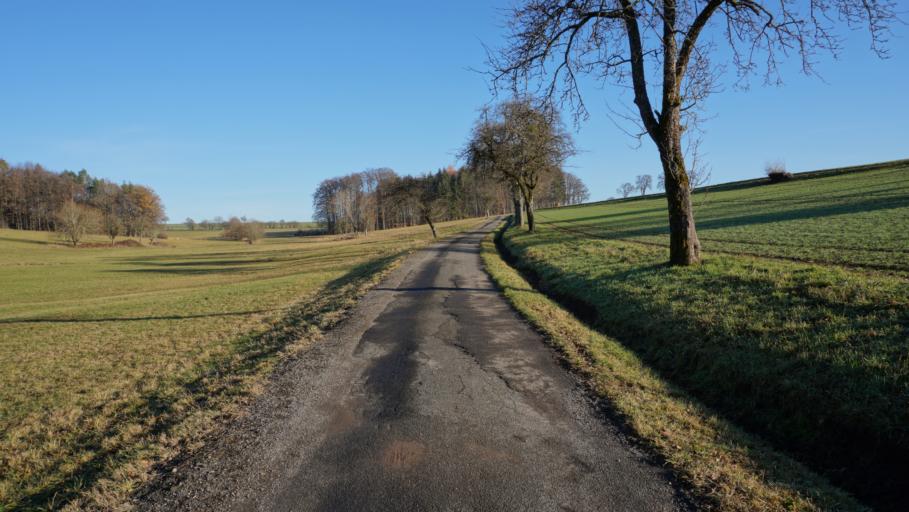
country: DE
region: Baden-Wuerttemberg
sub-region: Karlsruhe Region
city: Neckargerach
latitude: 49.4508
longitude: 9.0884
